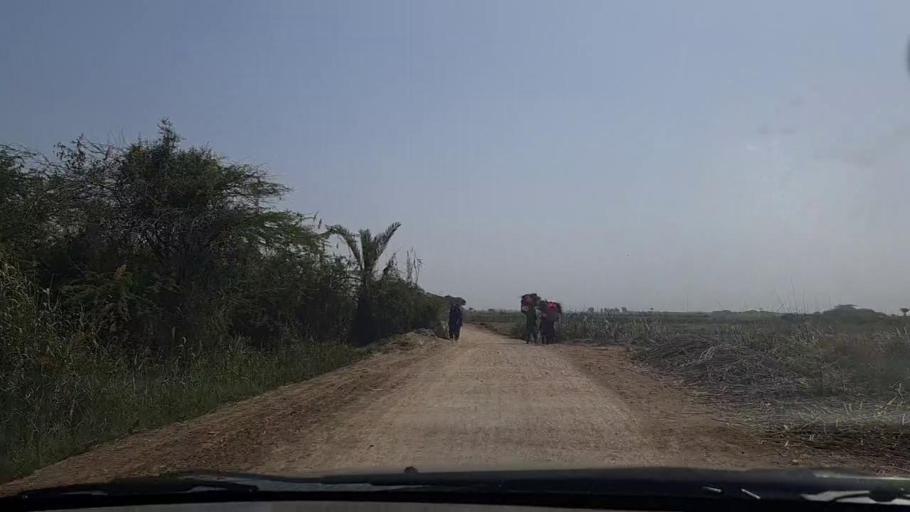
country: PK
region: Sindh
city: Keti Bandar
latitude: 24.2724
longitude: 67.6714
